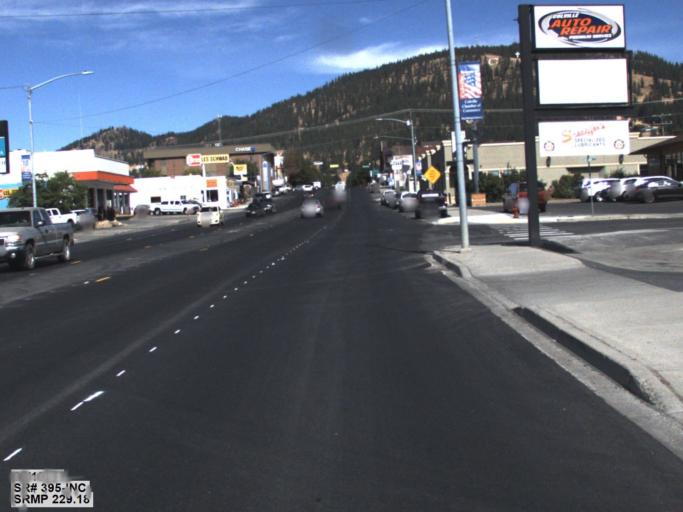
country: US
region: Washington
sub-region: Stevens County
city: Colville
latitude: 48.5399
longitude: -117.9057
